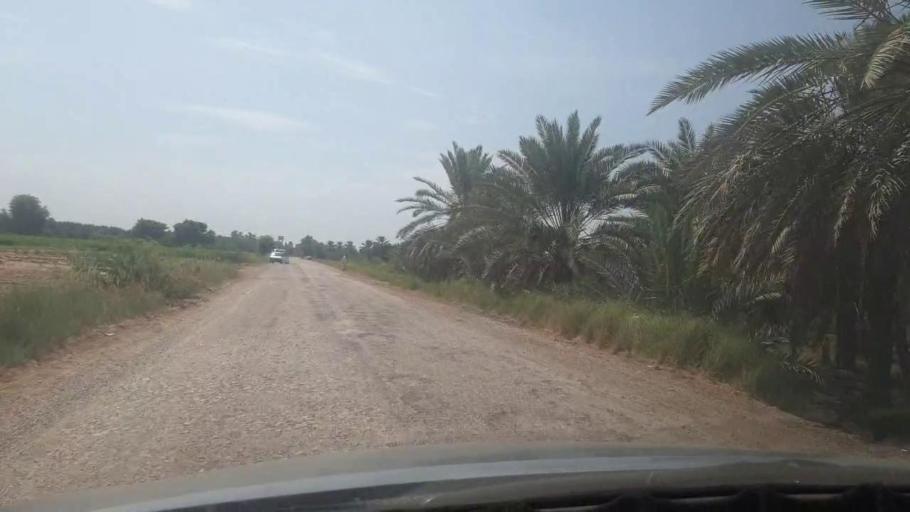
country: PK
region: Sindh
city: Bozdar
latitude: 27.2042
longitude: 68.5812
